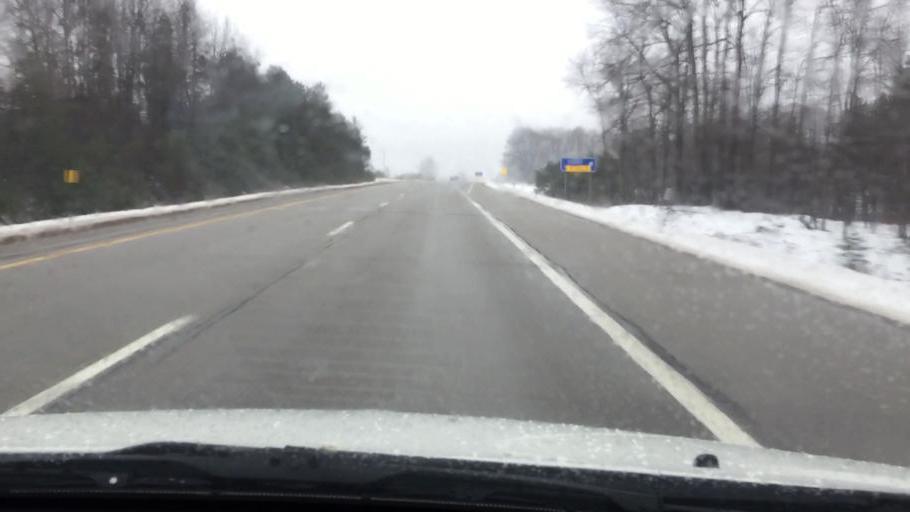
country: US
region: Michigan
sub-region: Wexford County
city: Cadillac
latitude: 44.1286
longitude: -85.4688
